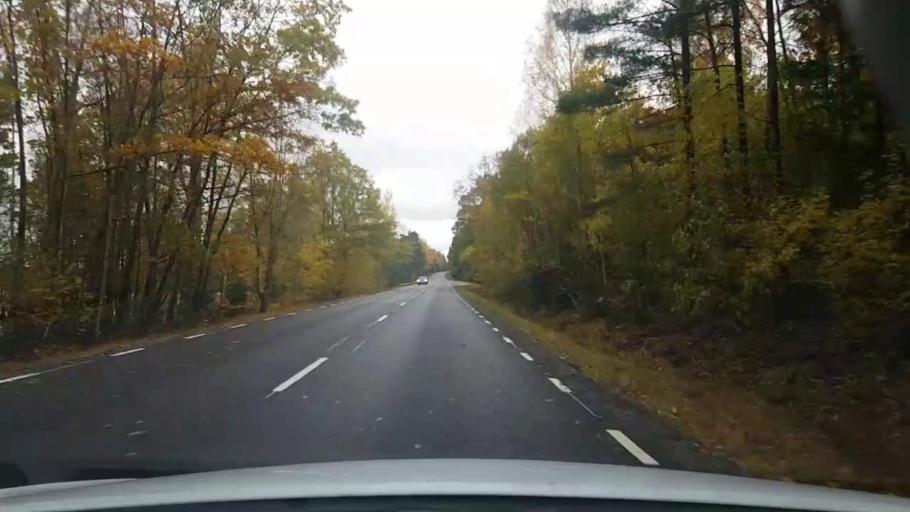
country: SE
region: OErebro
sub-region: Laxa Kommun
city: Laxa
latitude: 58.8362
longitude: 14.5467
